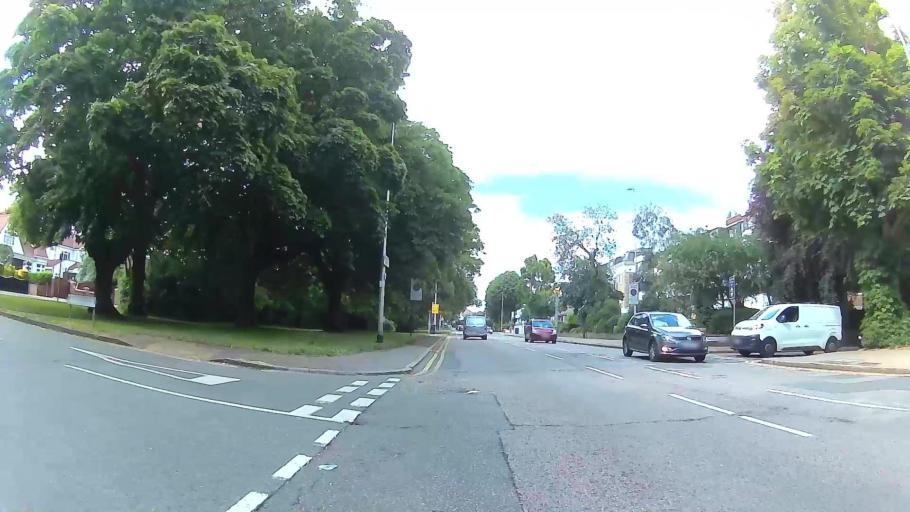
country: GB
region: England
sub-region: Greater London
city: Woodford Green
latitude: 51.5896
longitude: 0.0221
